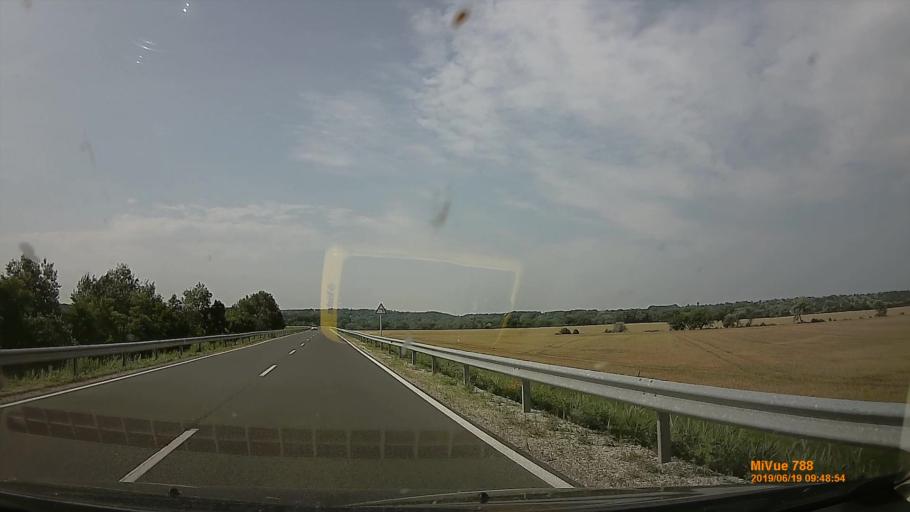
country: HU
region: Fejer
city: Adony
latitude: 47.0878
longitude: 18.8778
